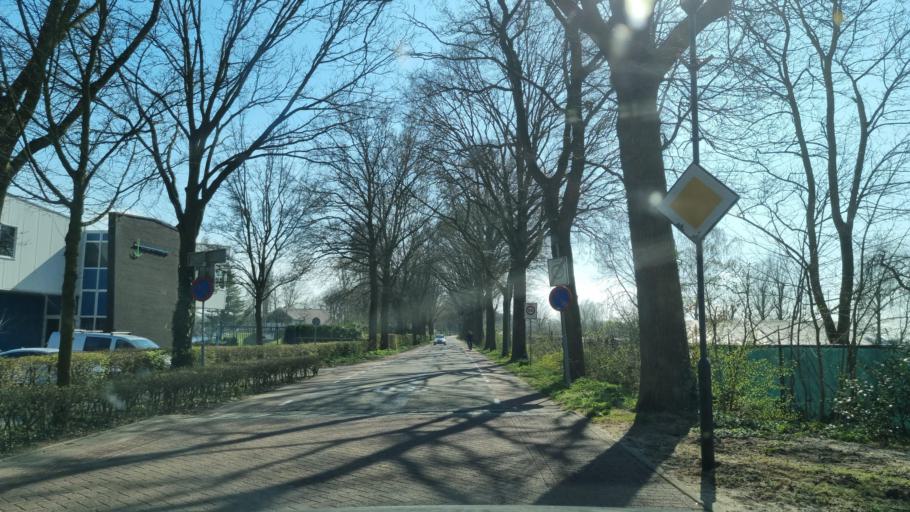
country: NL
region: Gelderland
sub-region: Gemeente Groesbeek
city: Bredeweg
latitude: 51.7356
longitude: 5.9175
